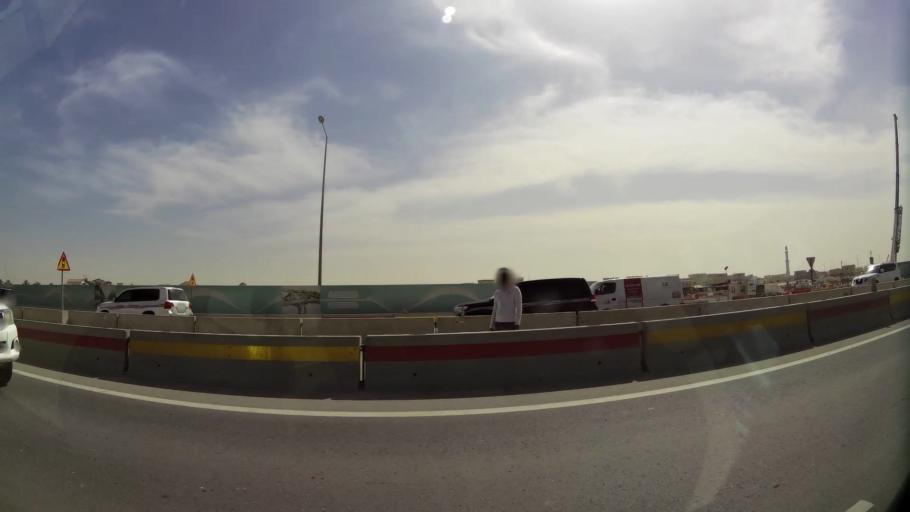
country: QA
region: Baladiyat ar Rayyan
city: Ar Rayyan
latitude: 25.3073
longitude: 51.4107
